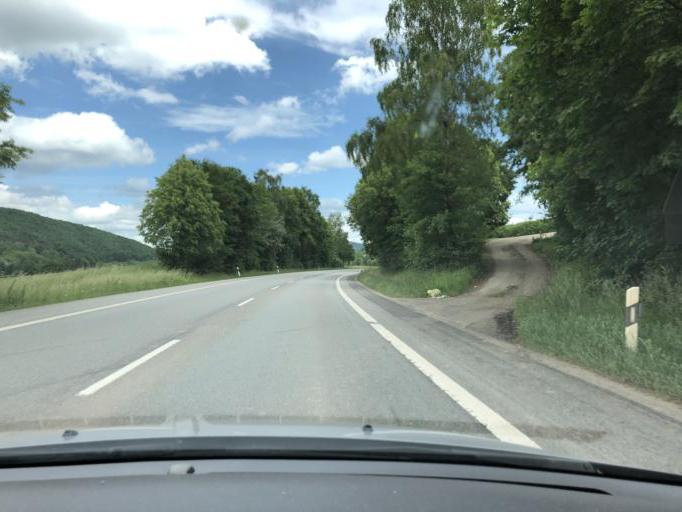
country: DE
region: Hesse
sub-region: Regierungsbezirk Kassel
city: Sontra
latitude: 51.0978
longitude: 9.9583
